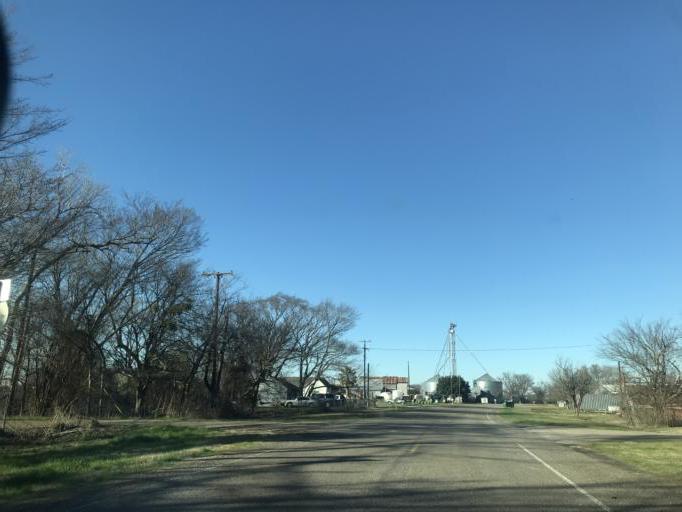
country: US
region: Texas
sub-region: Ellis County
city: Ferris
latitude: 32.4901
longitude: -96.6664
